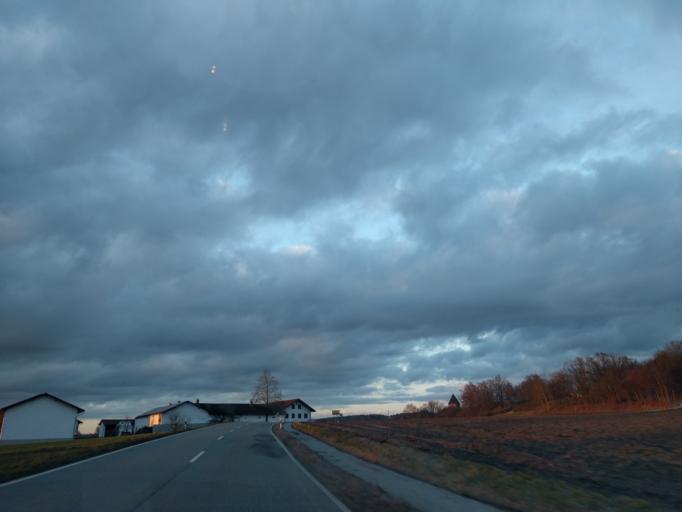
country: DE
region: Bavaria
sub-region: Lower Bavaria
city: Hofkirchen
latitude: 48.6818
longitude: 13.1171
